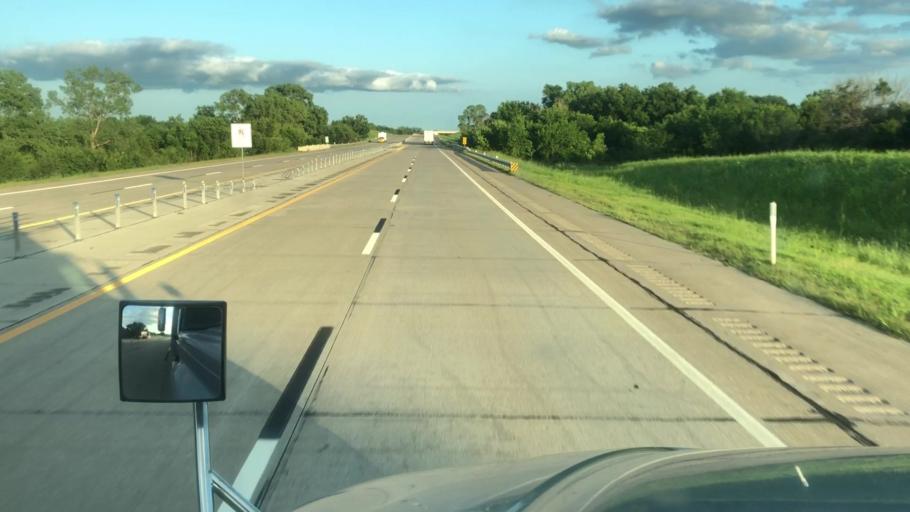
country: US
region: Oklahoma
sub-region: Pawnee County
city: Pawnee
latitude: 36.3255
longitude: -97.0048
